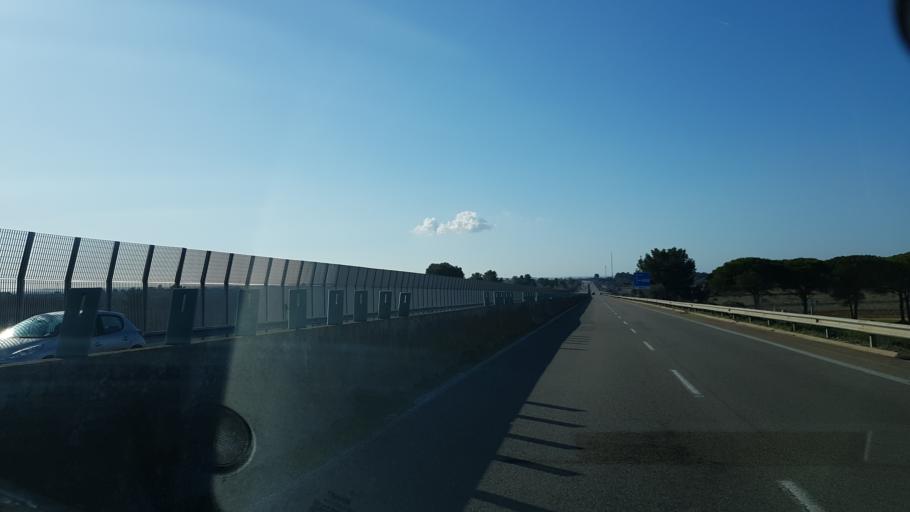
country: IT
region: Apulia
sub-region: Provincia di Lecce
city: Sannicola
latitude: 40.1116
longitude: 18.0403
